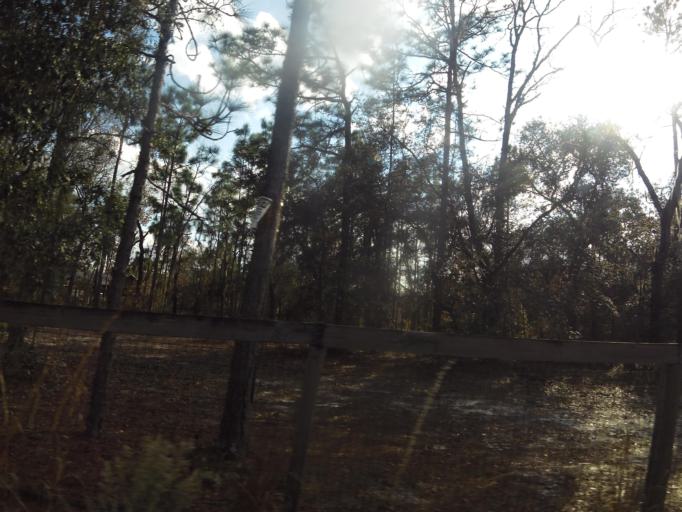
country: US
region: Florida
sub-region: Clay County
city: Middleburg
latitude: 30.1354
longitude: -81.9524
